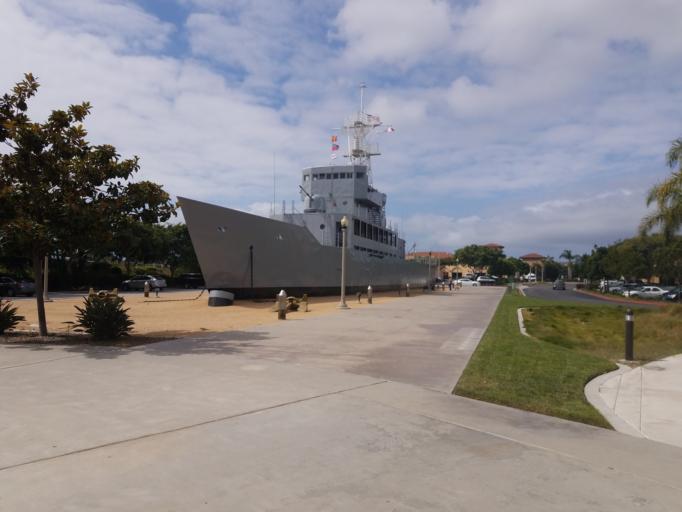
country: US
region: California
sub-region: San Diego County
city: Coronado
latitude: 32.7288
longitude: -117.2158
